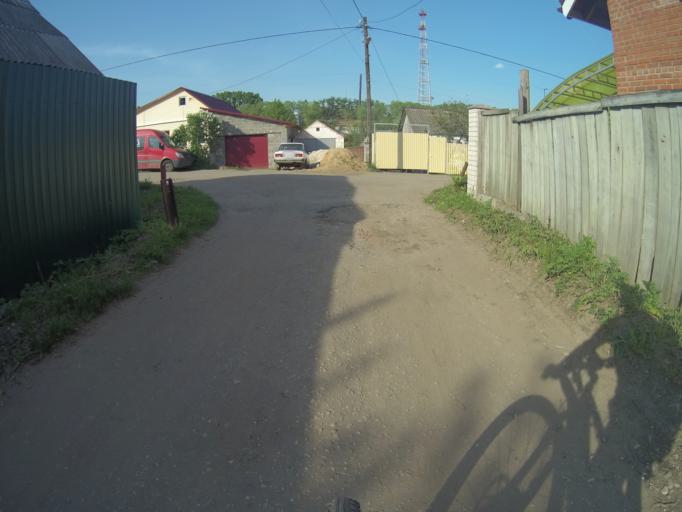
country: RU
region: Vladimir
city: Bogolyubovo
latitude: 56.1689
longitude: 40.4904
